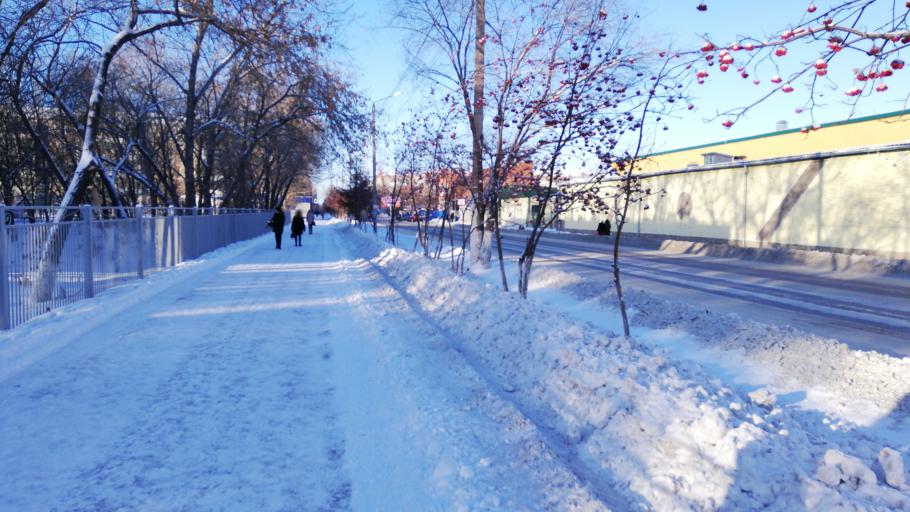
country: KZ
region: Soltustik Qazaqstan
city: Petropavlovsk
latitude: 54.8632
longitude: 69.1460
